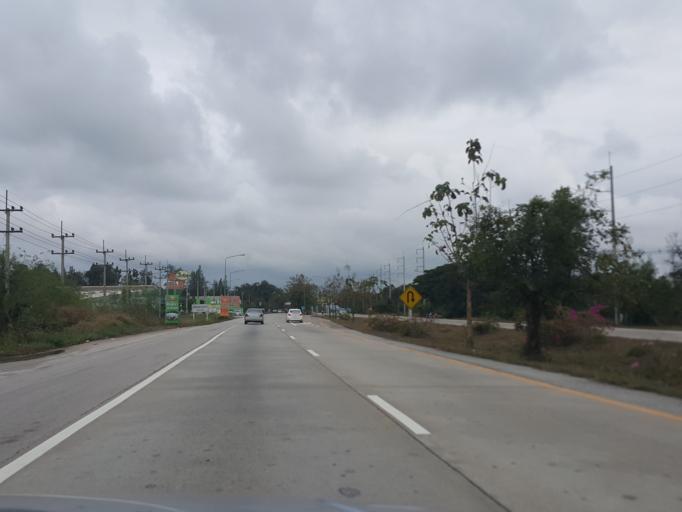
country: TH
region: Lampang
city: Hang Chat
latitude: 18.3135
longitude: 99.3837
